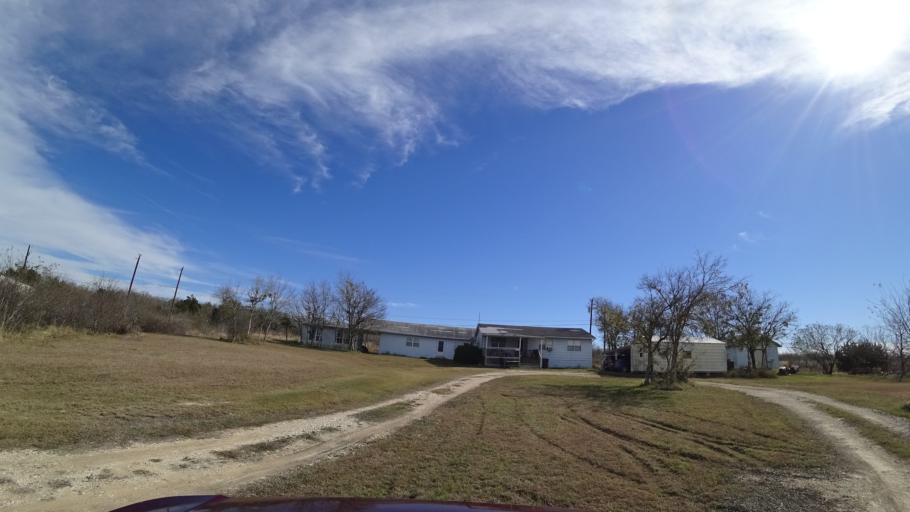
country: US
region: Texas
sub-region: Travis County
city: Onion Creek
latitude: 30.1153
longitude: -97.7104
